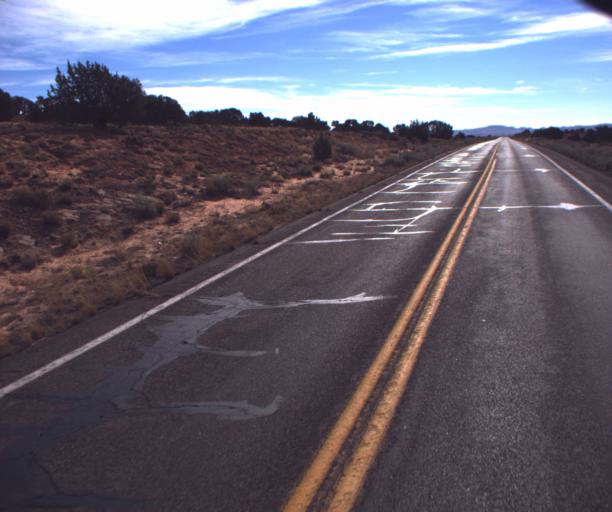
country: US
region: Arizona
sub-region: Coconino County
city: Kaibito
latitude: 36.6700
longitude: -111.2558
